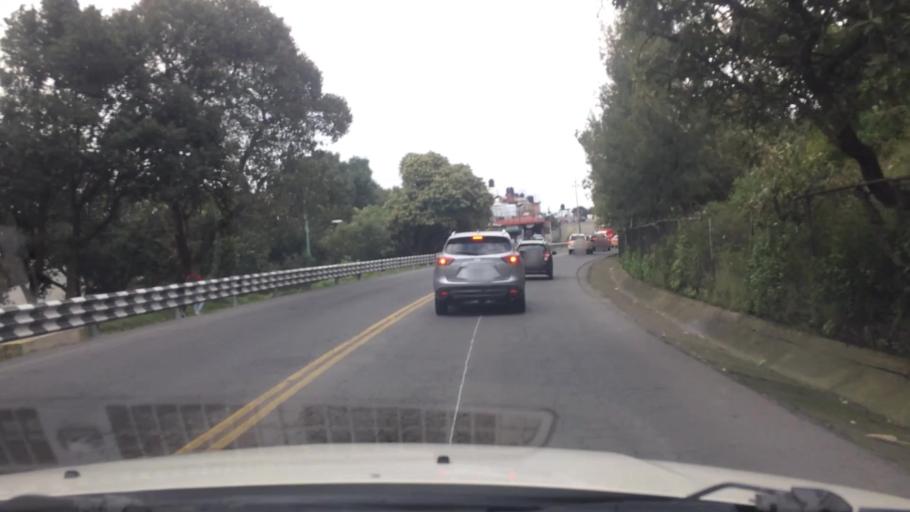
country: MX
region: Mexico City
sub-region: Tlalpan
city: Lomas de Tepemecatl
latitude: 19.2674
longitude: -99.2241
